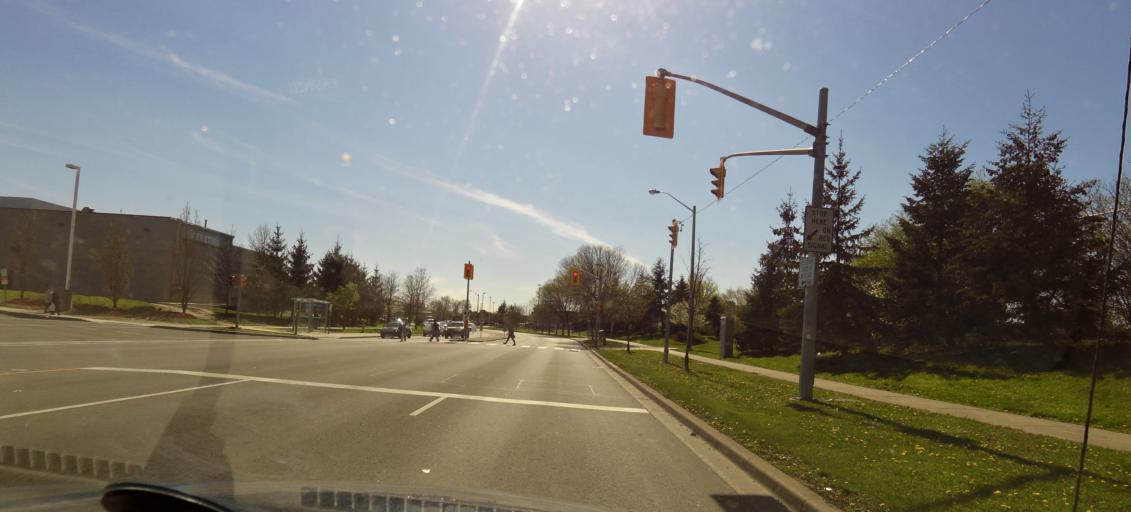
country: CA
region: Ontario
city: Etobicoke
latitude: 43.7434
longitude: -79.5867
